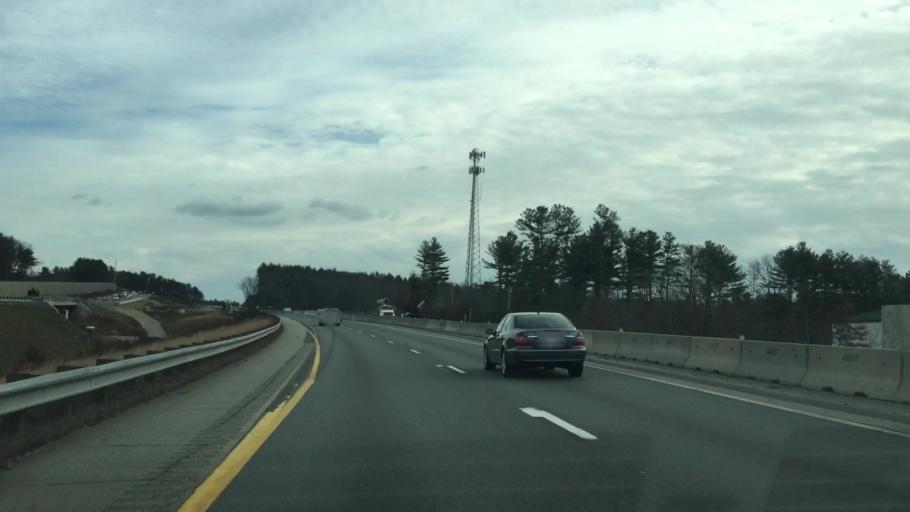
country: US
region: New Hampshire
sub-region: Rockingham County
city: Derry
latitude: 42.8604
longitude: -71.3332
